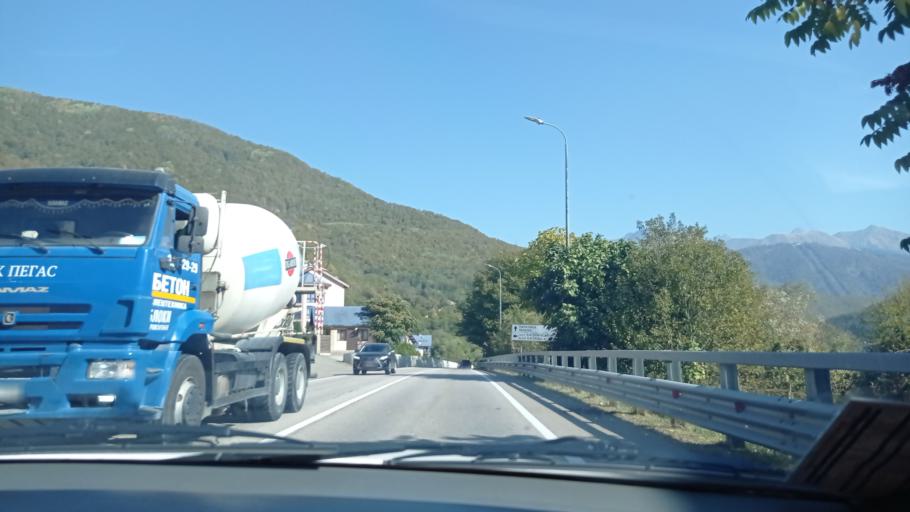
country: RU
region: Krasnodarskiy
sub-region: Sochi City
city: Krasnaya Polyana
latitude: 43.6829
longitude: 40.2240
